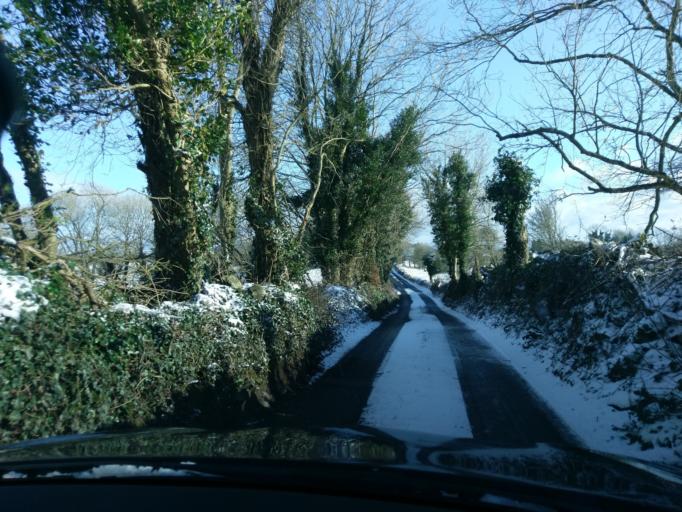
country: IE
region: Connaught
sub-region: County Galway
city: Athenry
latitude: 53.1994
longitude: -8.8014
